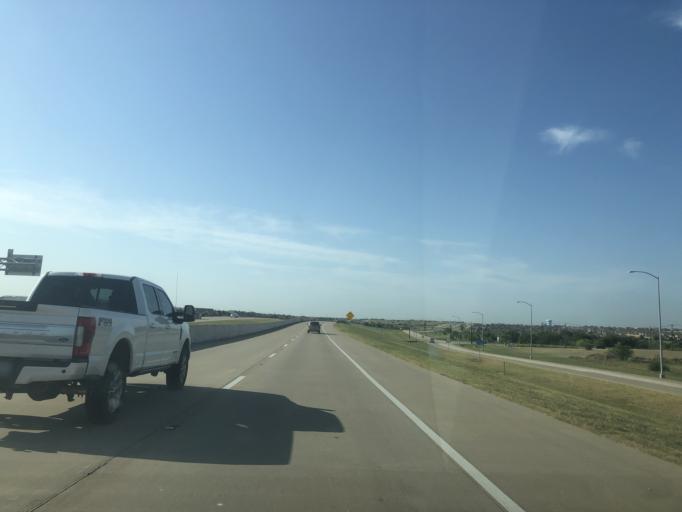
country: US
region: Texas
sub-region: Tarrant County
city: Benbrook
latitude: 32.6322
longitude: -97.4141
